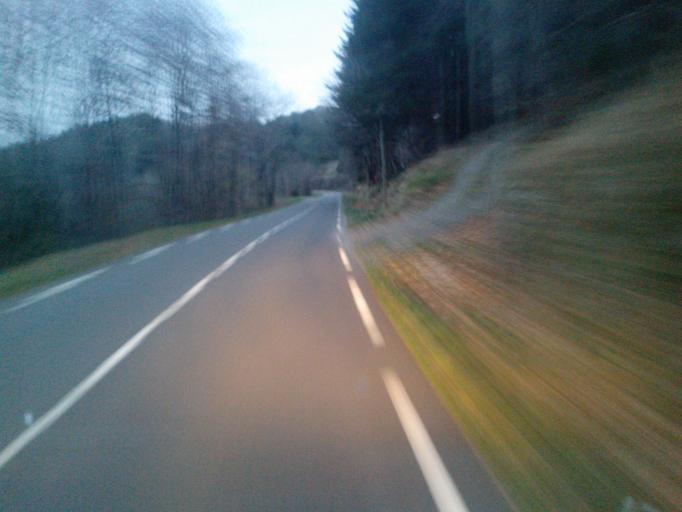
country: FR
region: Languedoc-Roussillon
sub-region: Departement du Gard
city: Saint-Jean-du-Gard
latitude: 44.1300
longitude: 3.7981
